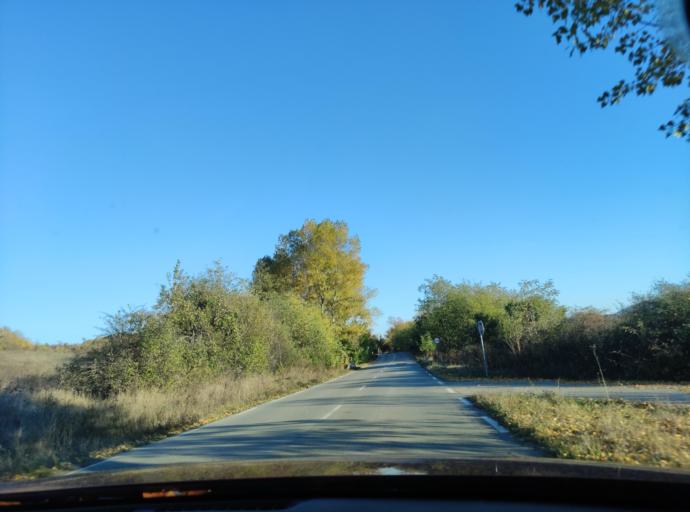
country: BG
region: Montana
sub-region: Obshtina Chiprovtsi
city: Chiprovtsi
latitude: 43.4304
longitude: 22.9937
